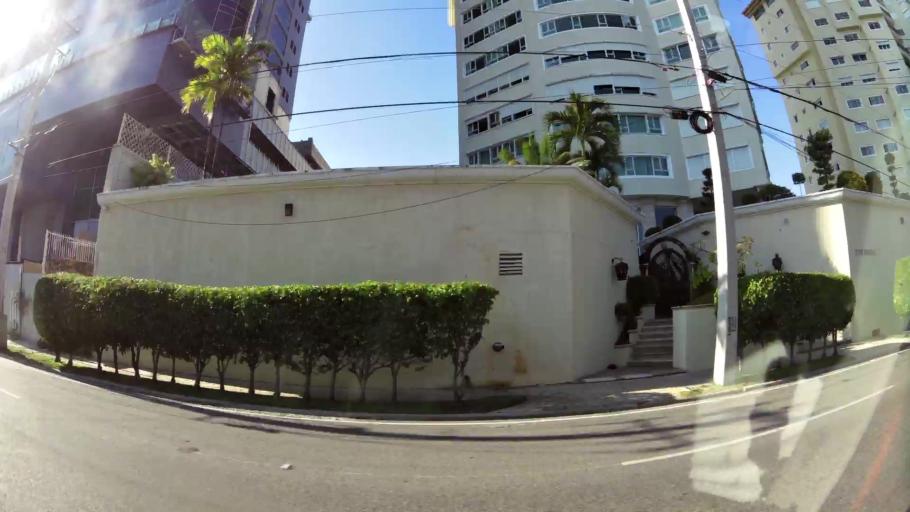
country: DO
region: Nacional
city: Bella Vista
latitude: 18.4382
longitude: -69.9704
